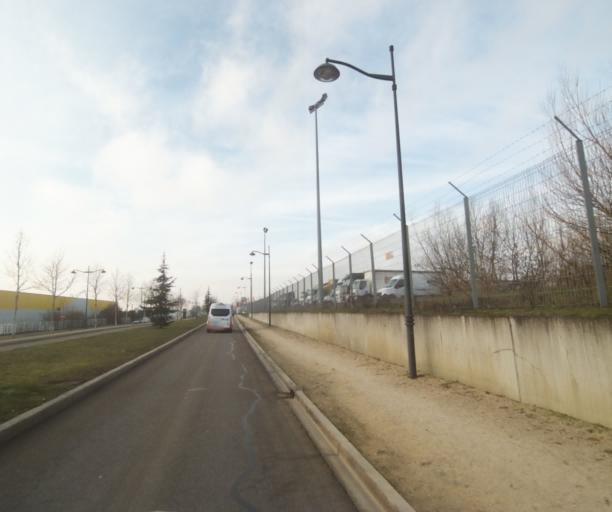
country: FR
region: Champagne-Ardenne
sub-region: Departement de la Haute-Marne
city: Bettancourt-la-Ferree
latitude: 48.6538
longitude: 4.9649
